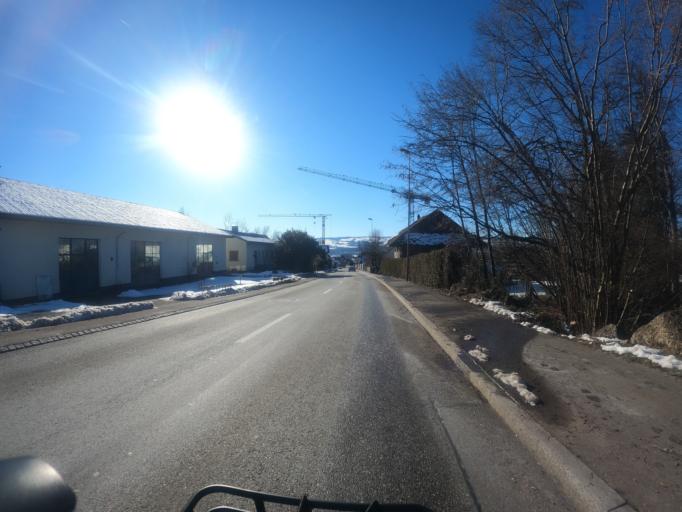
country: CH
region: Zurich
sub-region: Bezirk Affoltern
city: Ottenbach
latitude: 47.2841
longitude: 8.4089
